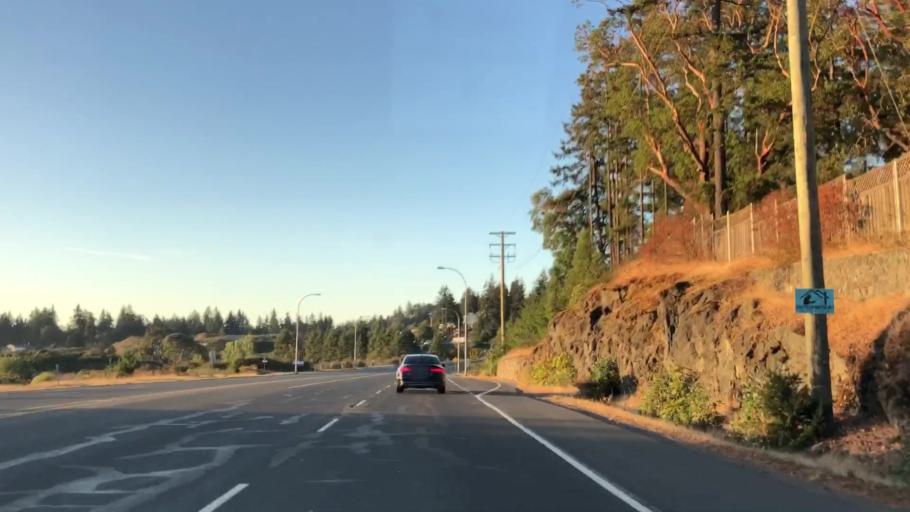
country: CA
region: British Columbia
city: Colwood
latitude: 48.4286
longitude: -123.5025
